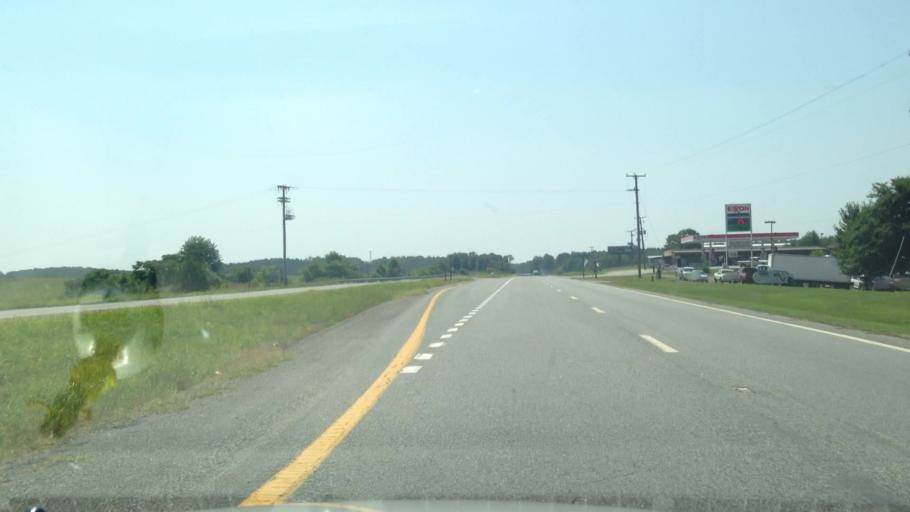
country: US
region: Virginia
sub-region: Patrick County
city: Patrick Springs
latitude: 36.6002
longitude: -80.1591
